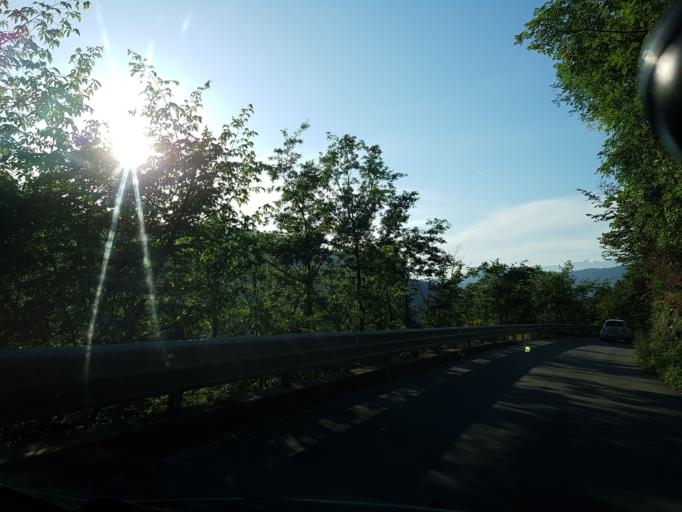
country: IT
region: Tuscany
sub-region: Provincia di Lucca
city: Minucciano
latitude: 44.1752
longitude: 10.2003
